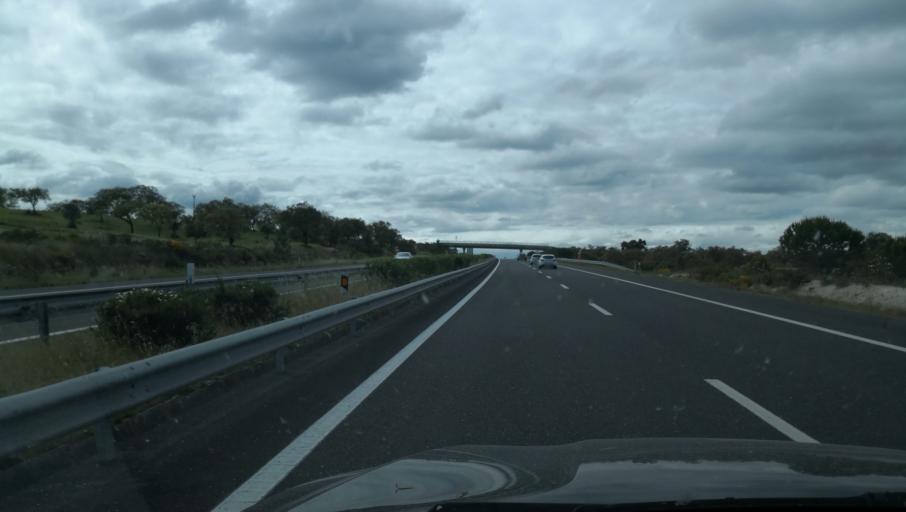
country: PT
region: Santarem
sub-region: Benavente
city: Poceirao
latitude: 38.8431
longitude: -8.7380
